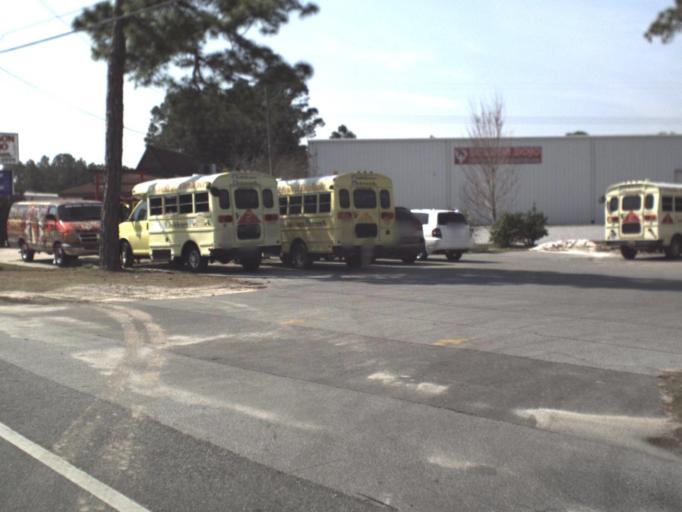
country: US
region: Florida
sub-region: Bay County
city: Lynn Haven
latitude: 30.2190
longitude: -85.6658
